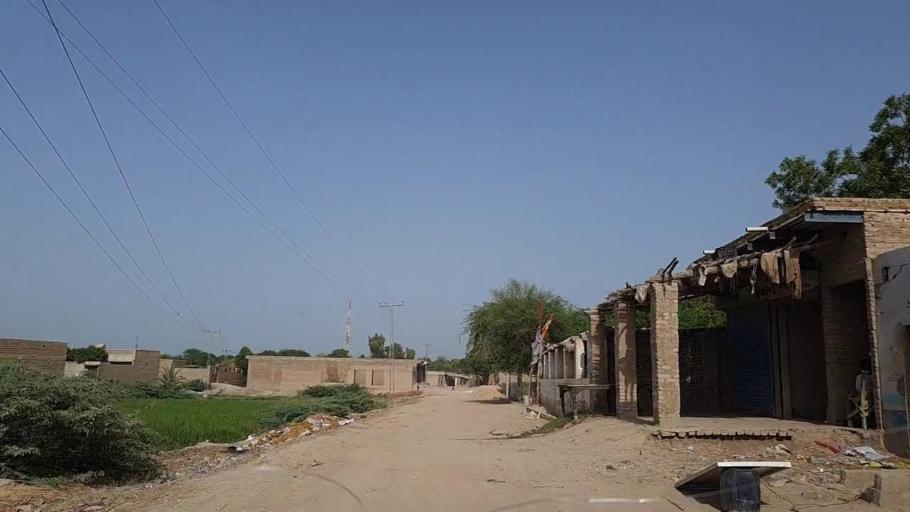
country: PK
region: Sindh
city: Kandiaro
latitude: 27.0650
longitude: 68.2043
